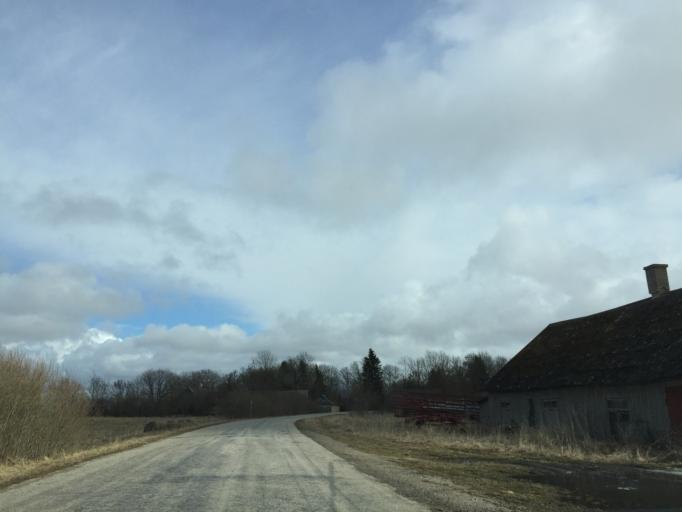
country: EE
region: Laeaene
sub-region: Lihula vald
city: Lihula
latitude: 58.7348
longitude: 23.8525
